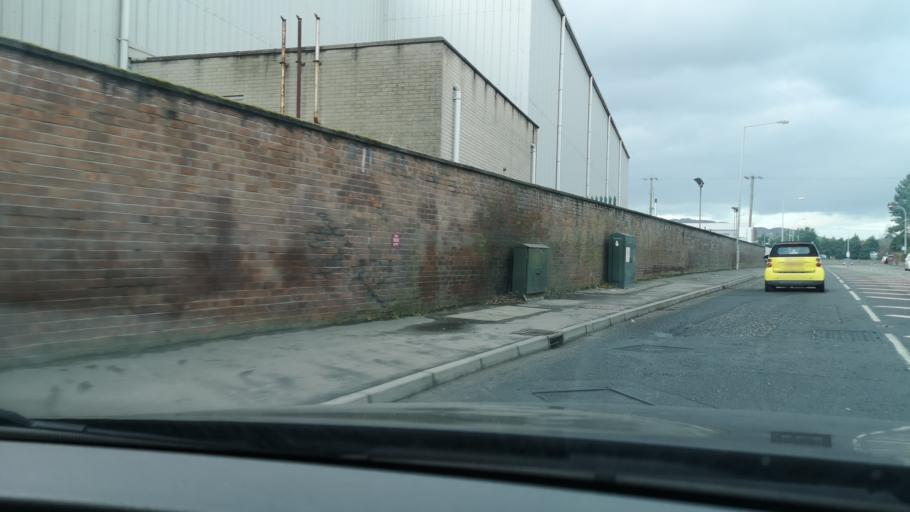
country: GB
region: Northern Ireland
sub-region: Down District
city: Warrenpoint
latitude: 54.1021
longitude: -6.2581
